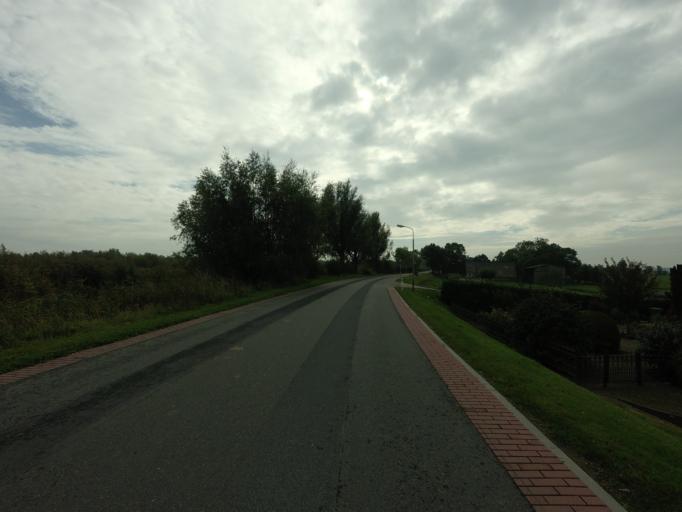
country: NL
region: Utrecht
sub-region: Gemeente Lopik
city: Lopik
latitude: 51.9407
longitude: 4.9961
